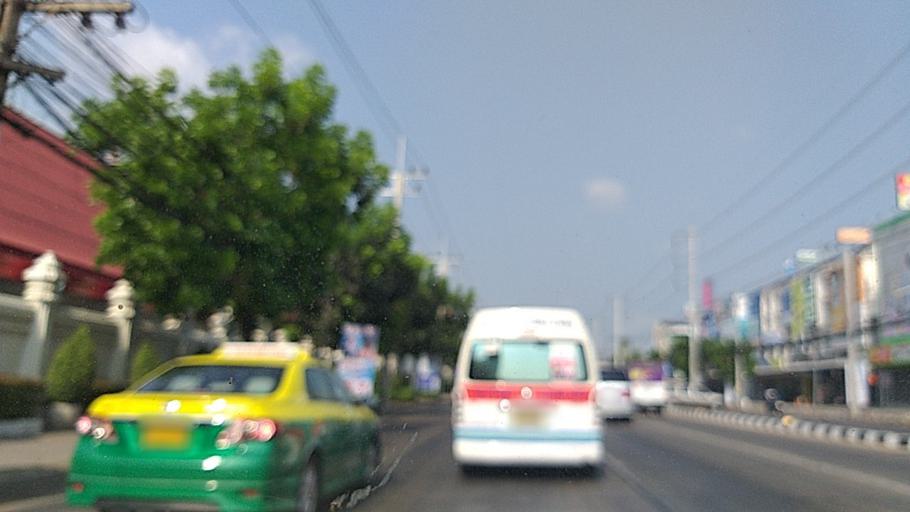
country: TH
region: Bangkok
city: Sai Mai
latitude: 13.9320
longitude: 100.6591
